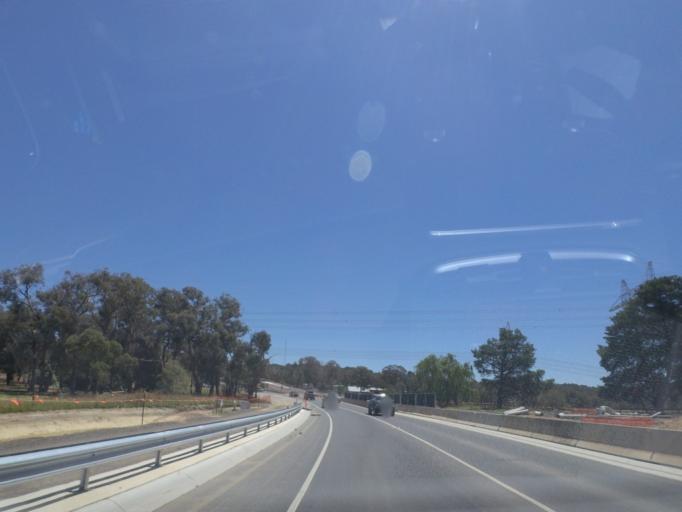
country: AU
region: Victoria
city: Plenty
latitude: -37.6576
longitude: 145.1255
